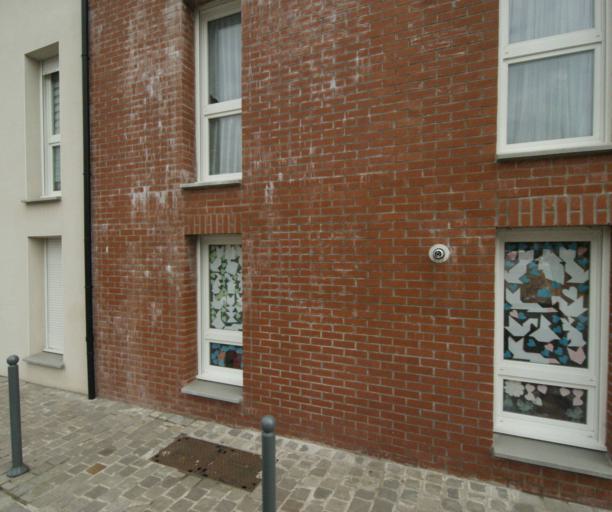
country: FR
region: Nord-Pas-de-Calais
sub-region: Departement du Nord
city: Salome
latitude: 50.5353
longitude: 2.8414
